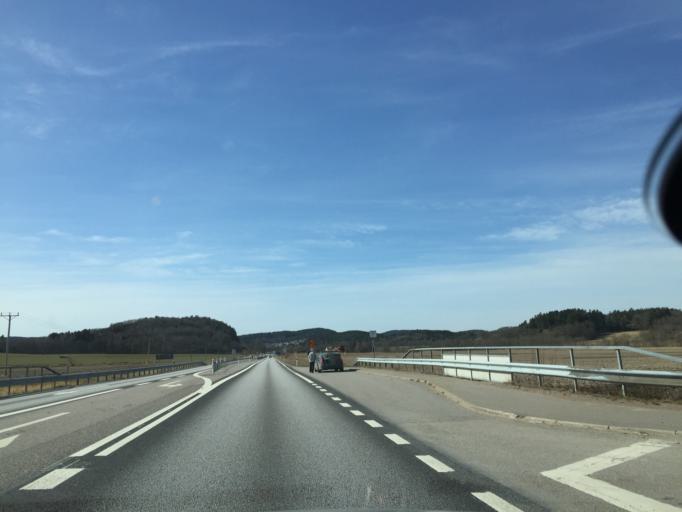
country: SE
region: Vaestra Goetaland
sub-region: Orust
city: Henan
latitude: 58.3462
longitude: 11.7792
